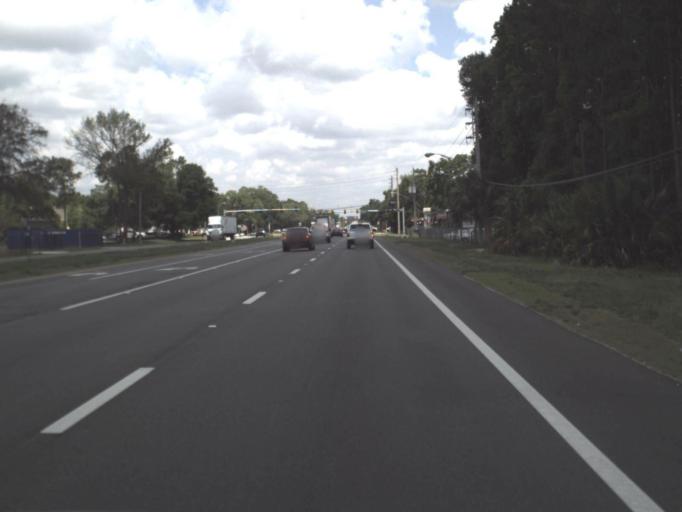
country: US
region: Florida
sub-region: Saint Johns County
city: Fruit Cove
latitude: 30.2042
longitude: -81.5754
